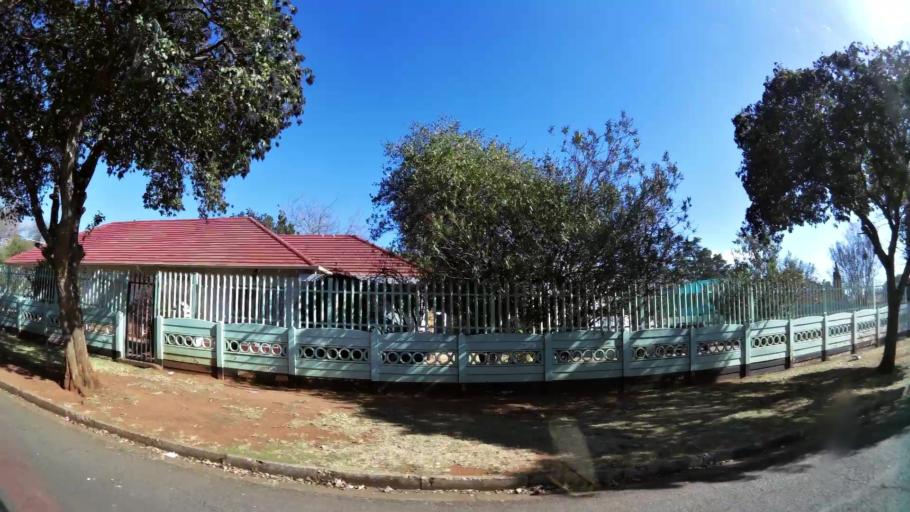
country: ZA
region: Gauteng
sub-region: West Rand District Municipality
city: Carletonville
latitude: -26.3616
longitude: 27.4004
